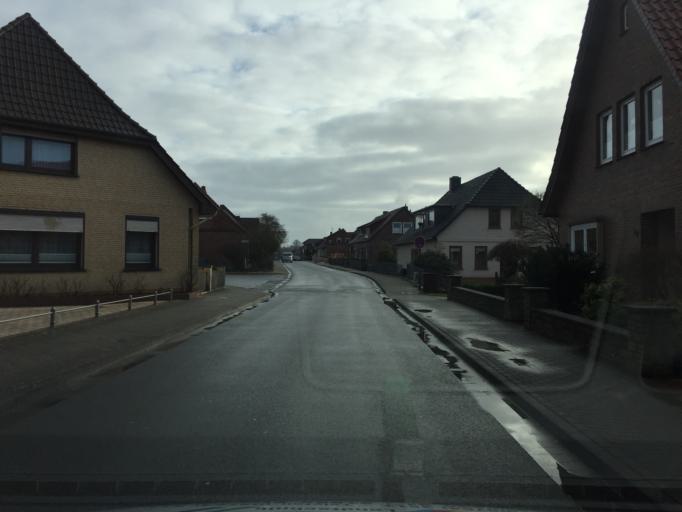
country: DE
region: Lower Saxony
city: Sulingen
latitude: 52.6806
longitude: 8.8073
